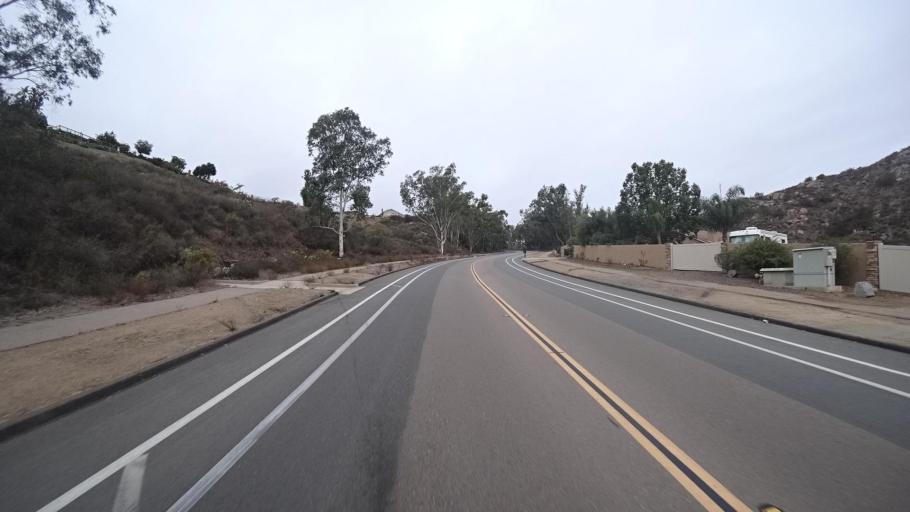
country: US
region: California
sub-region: San Diego County
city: Rancho San Diego
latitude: 32.7594
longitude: -116.9060
